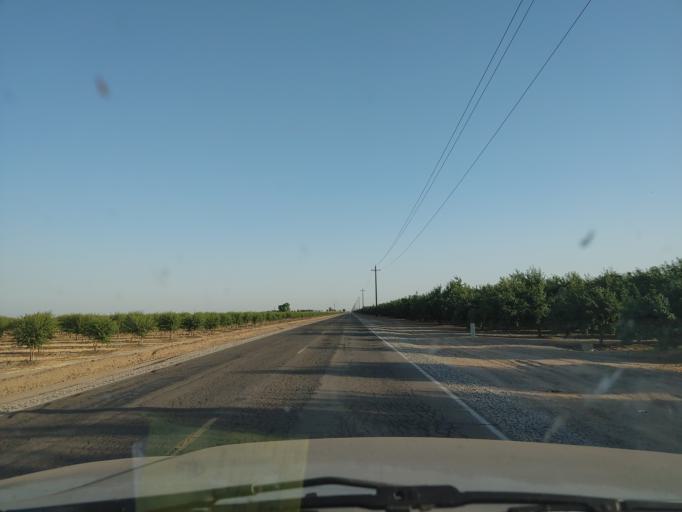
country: US
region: California
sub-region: Madera County
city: Chowchilla
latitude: 37.1490
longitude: -120.3829
